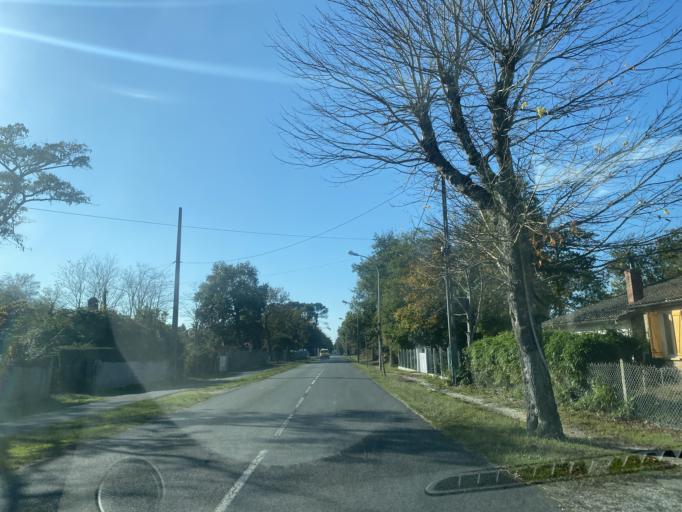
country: FR
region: Aquitaine
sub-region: Departement de la Gironde
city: Hourtin
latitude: 45.1828
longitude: -1.0736
